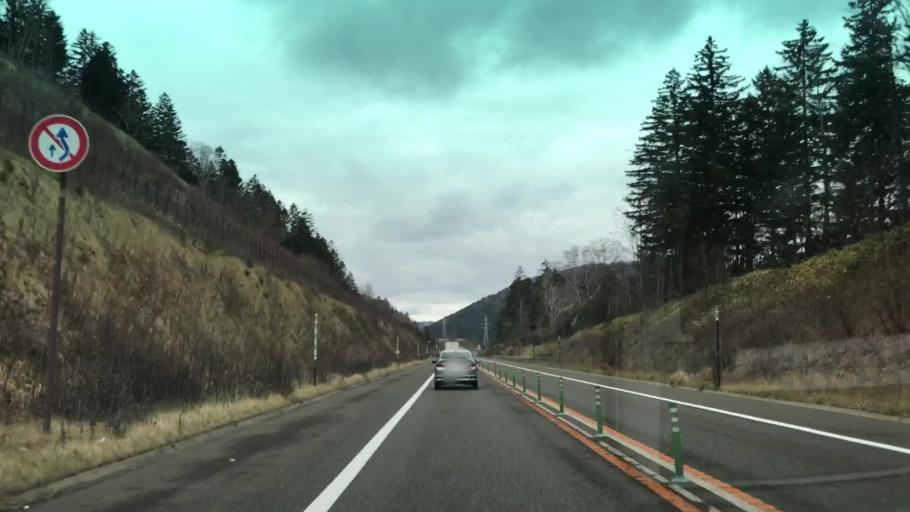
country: JP
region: Hokkaido
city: Shimo-furano
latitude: 43.0526
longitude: 142.6186
